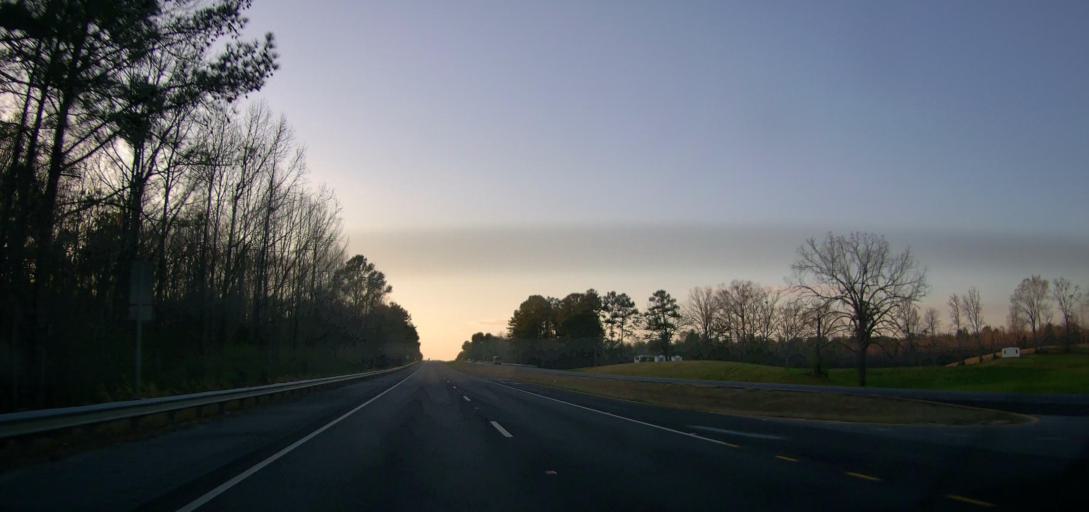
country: US
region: Alabama
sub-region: Coosa County
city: Stewartville
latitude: 33.1025
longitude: -86.2249
